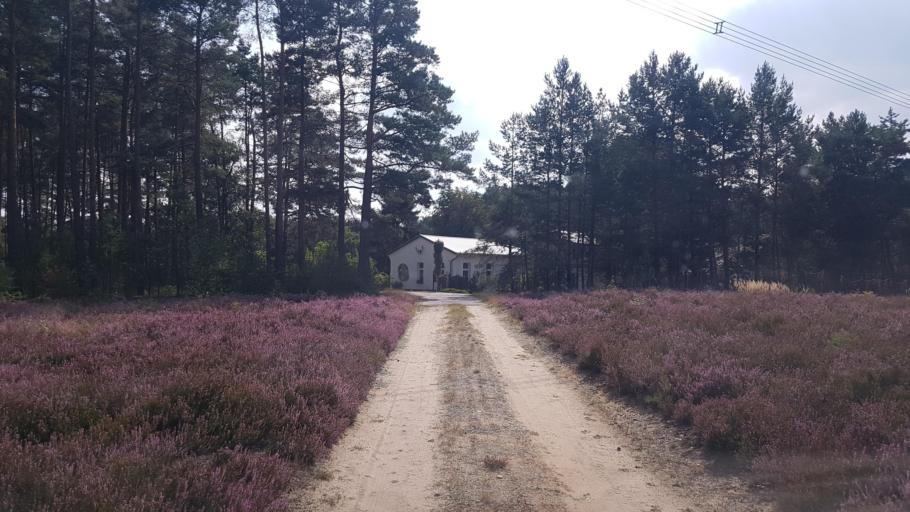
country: DE
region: Brandenburg
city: Hohenbucko
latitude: 51.7586
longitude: 13.5408
